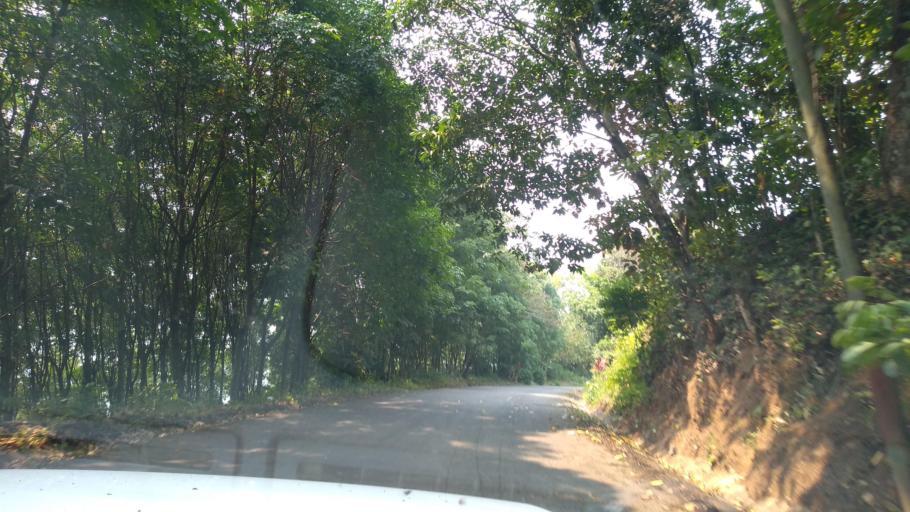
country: MX
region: Veracruz
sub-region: Tezonapa
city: Laguna Chica (Pueblo Nuevo)
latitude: 18.5312
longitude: -96.7883
